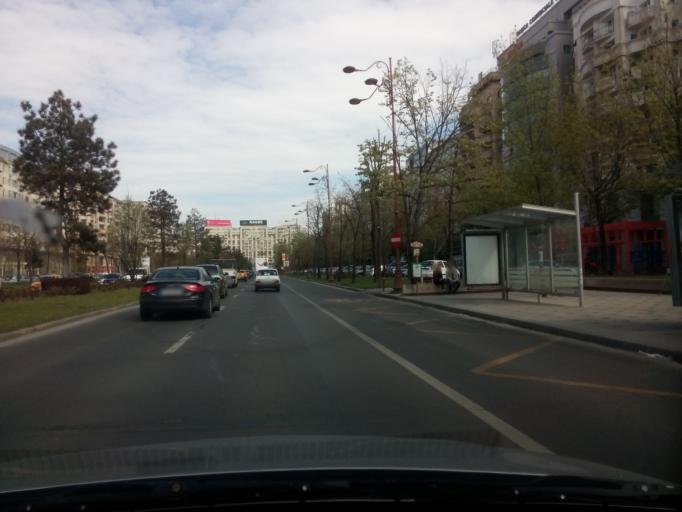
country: RO
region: Bucuresti
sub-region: Municipiul Bucuresti
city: Bucharest
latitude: 44.4258
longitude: 26.1236
